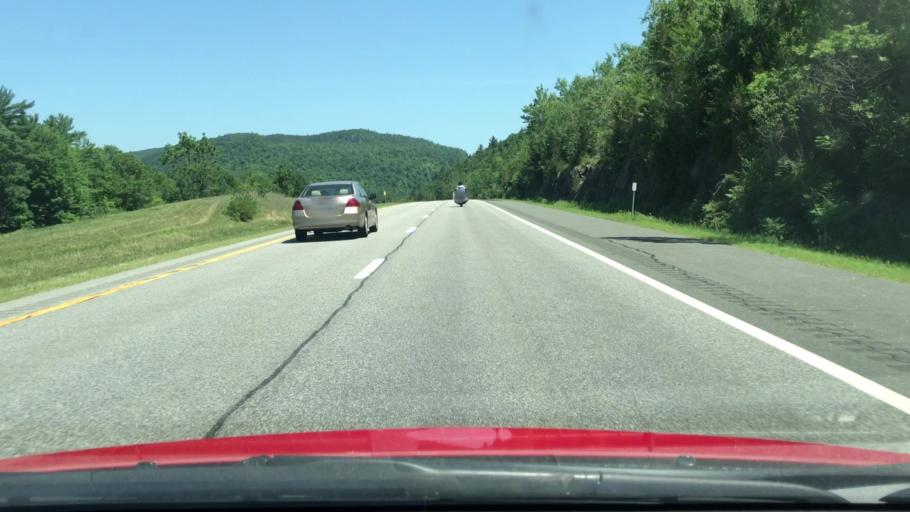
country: US
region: New York
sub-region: Essex County
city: Keeseville
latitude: 44.3797
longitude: -73.5155
